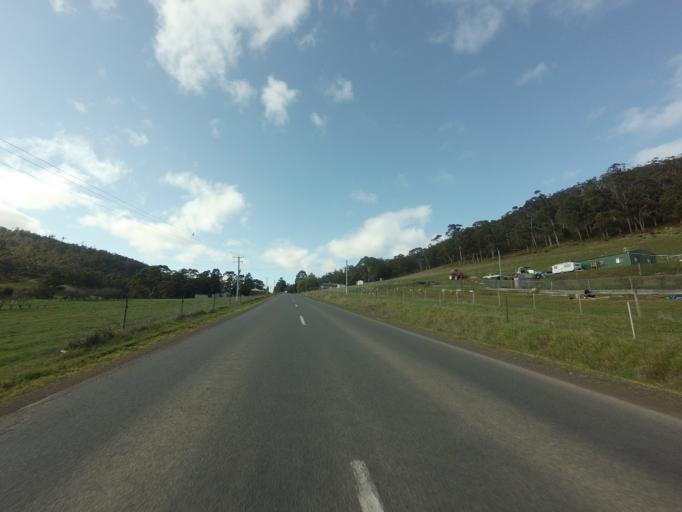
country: AU
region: Tasmania
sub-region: Huon Valley
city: Geeveston
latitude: -43.1742
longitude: 146.9458
